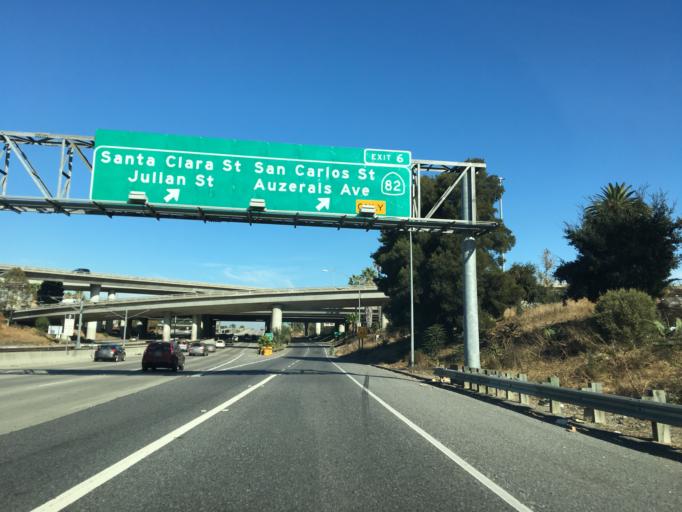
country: US
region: California
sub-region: Santa Clara County
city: San Jose
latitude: 37.3221
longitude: -121.8909
